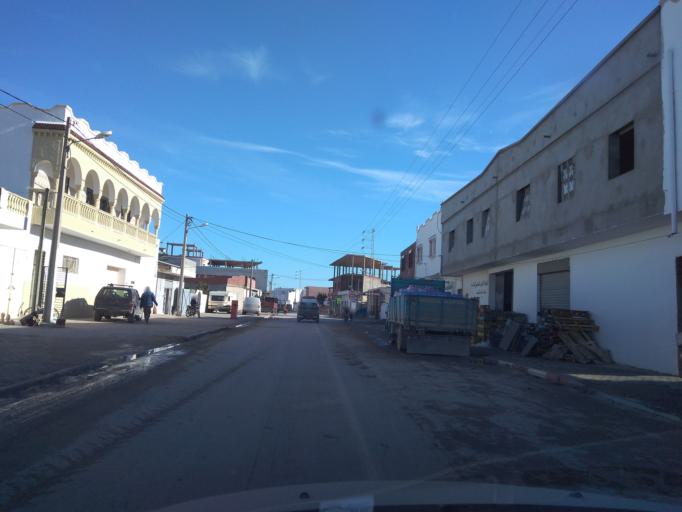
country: TN
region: Ariana
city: Qal'at al Andalus
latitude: 37.0614
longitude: 10.1240
